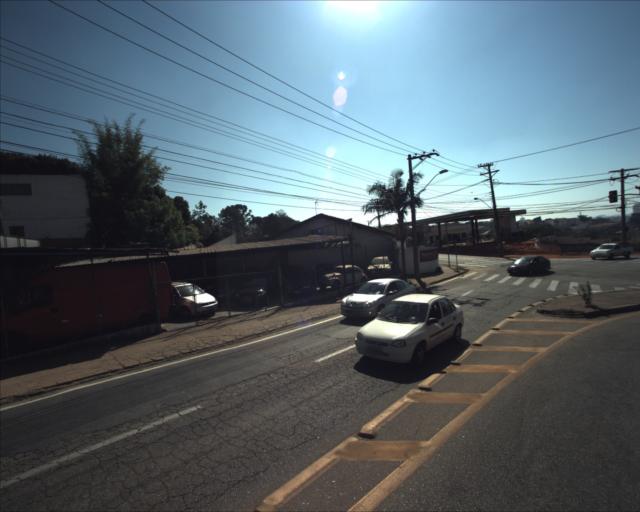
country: BR
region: Sao Paulo
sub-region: Sorocaba
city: Sorocaba
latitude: -23.5027
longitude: -47.4813
